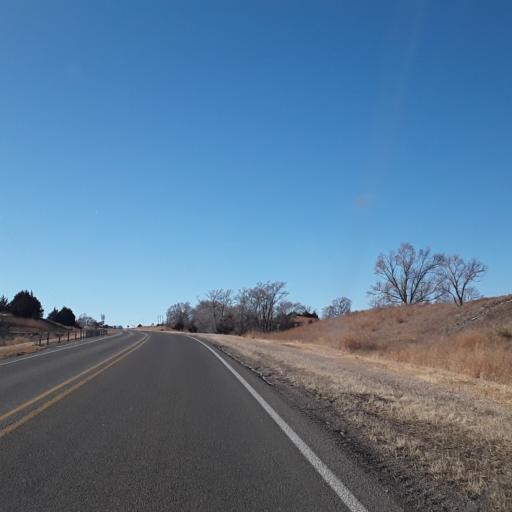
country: US
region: Nebraska
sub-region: Frontier County
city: Stockville
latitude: 40.6576
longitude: -100.6288
